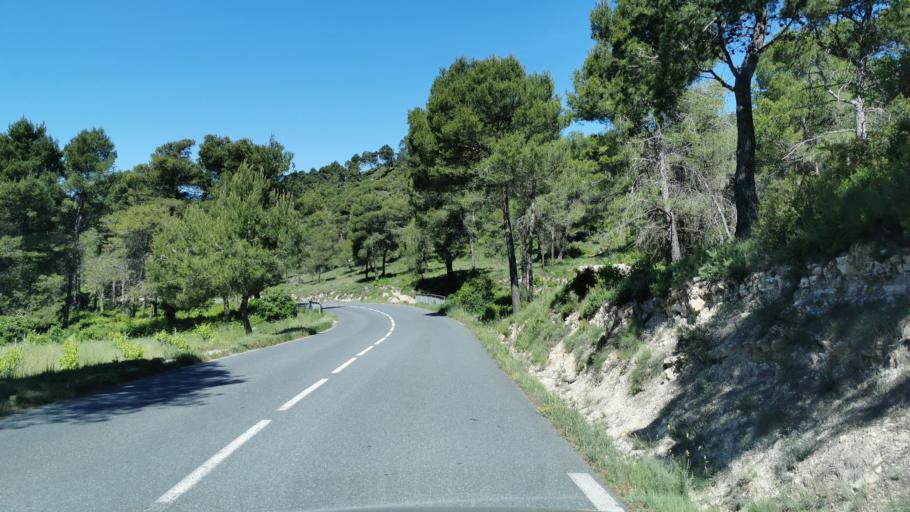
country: FR
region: Languedoc-Roussillon
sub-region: Departement de l'Aude
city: Armissan
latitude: 43.1748
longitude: 3.0826
